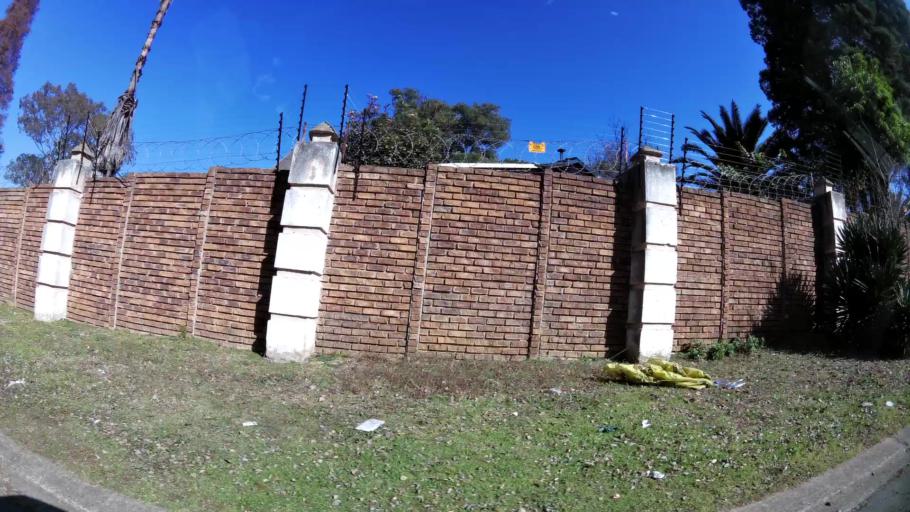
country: ZA
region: Gauteng
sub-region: City of Johannesburg Metropolitan Municipality
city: Modderfontein
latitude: -26.1179
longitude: 28.1097
